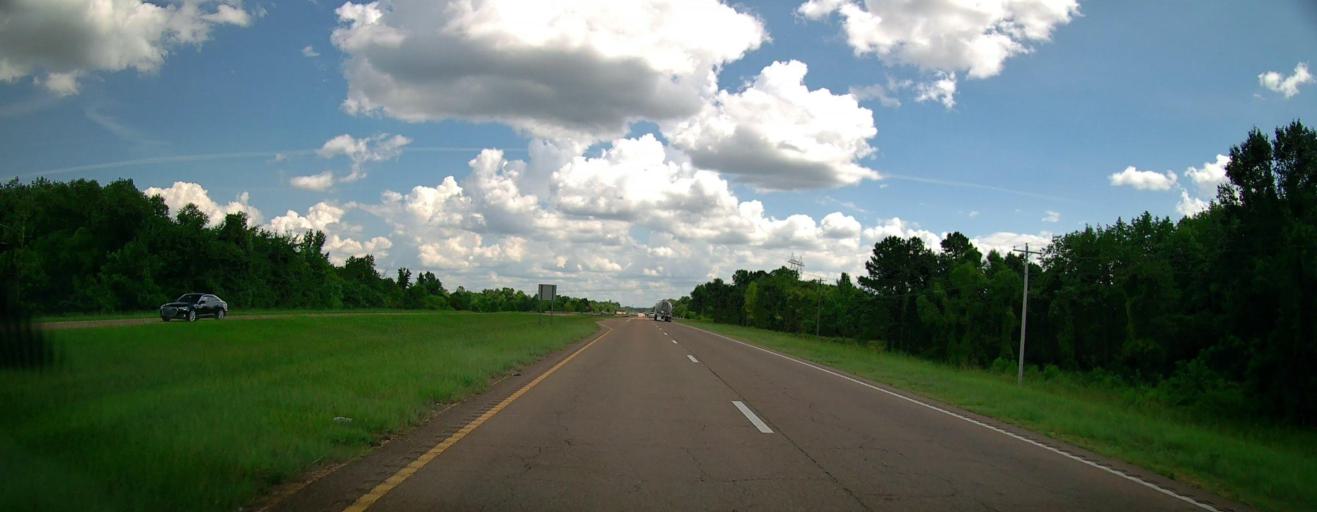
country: US
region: Mississippi
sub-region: Lowndes County
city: Columbus Air Force Base
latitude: 33.6822
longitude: -88.4341
